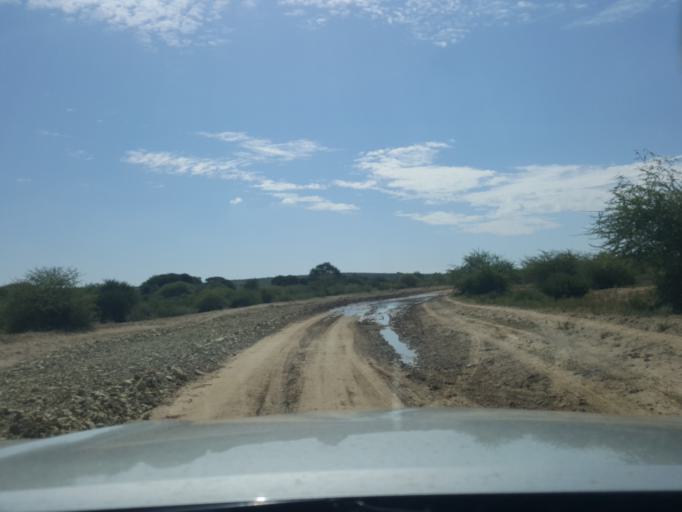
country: BW
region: Kweneng
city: Letlhakeng
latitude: -23.9862
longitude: 24.9695
